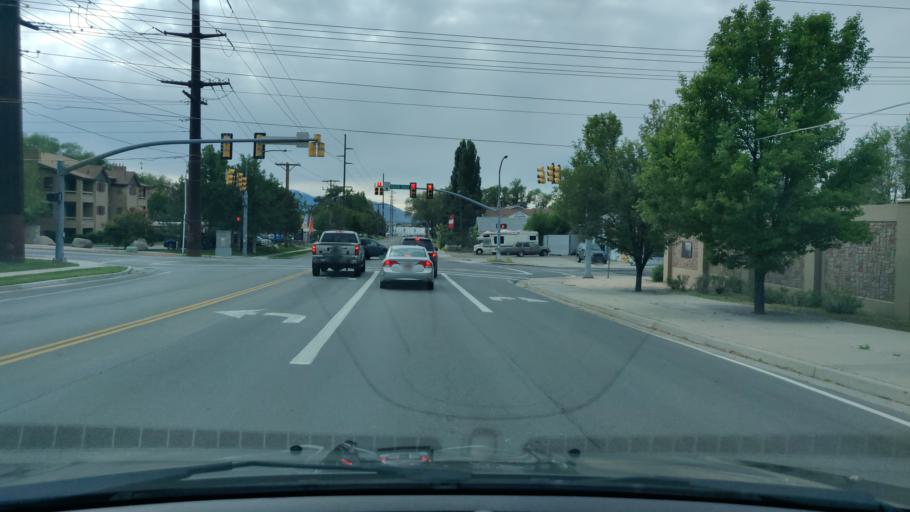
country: US
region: Utah
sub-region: Salt Lake County
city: Little Cottonwood Creek Valley
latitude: 40.6189
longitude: -111.8614
